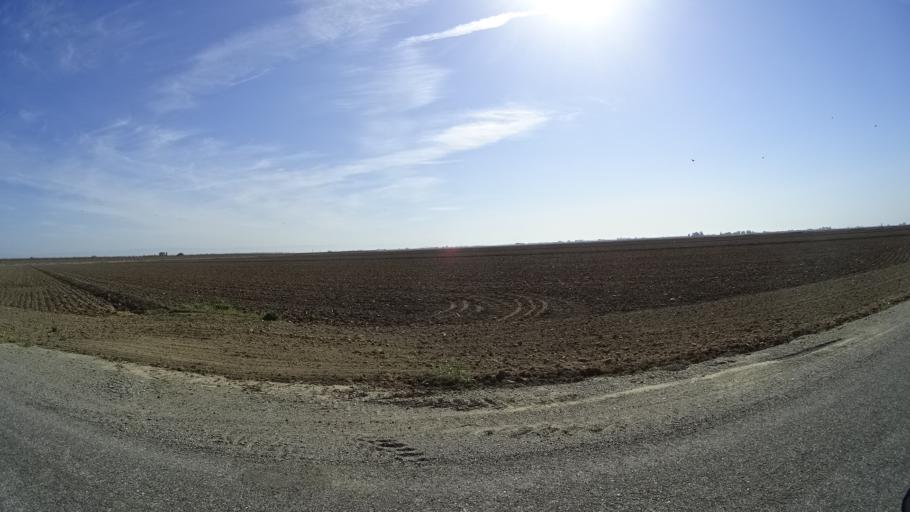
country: US
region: California
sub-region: Glenn County
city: Willows
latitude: 39.6151
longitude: -122.1170
